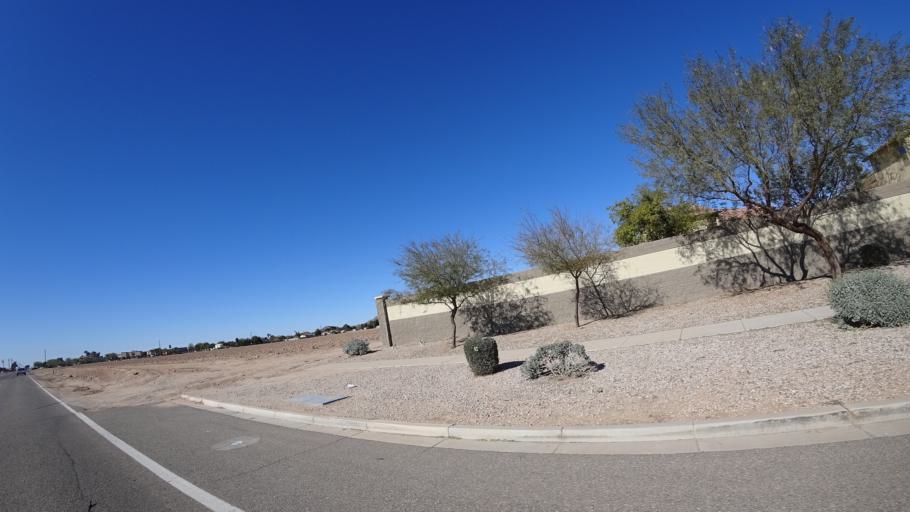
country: US
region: Arizona
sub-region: Maricopa County
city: Buckeye
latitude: 33.4067
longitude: -112.5864
